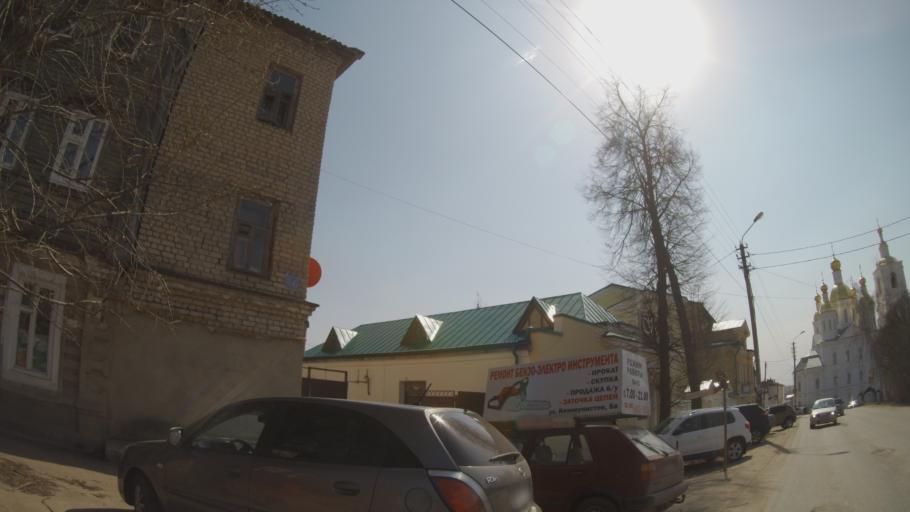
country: RU
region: Nizjnij Novgorod
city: Arzamas
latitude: 55.3861
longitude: 43.8186
